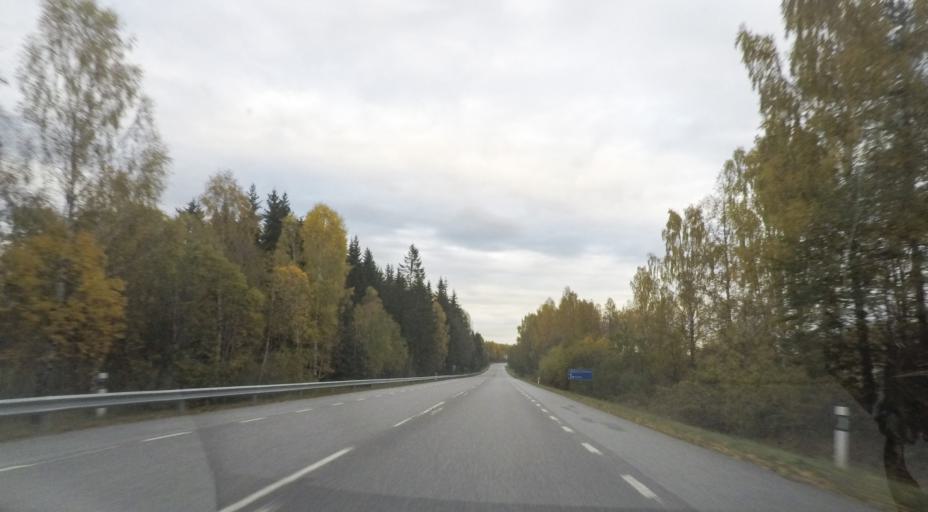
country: SE
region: OErebro
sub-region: Nora Kommun
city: Nora
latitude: 59.5081
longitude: 15.0076
